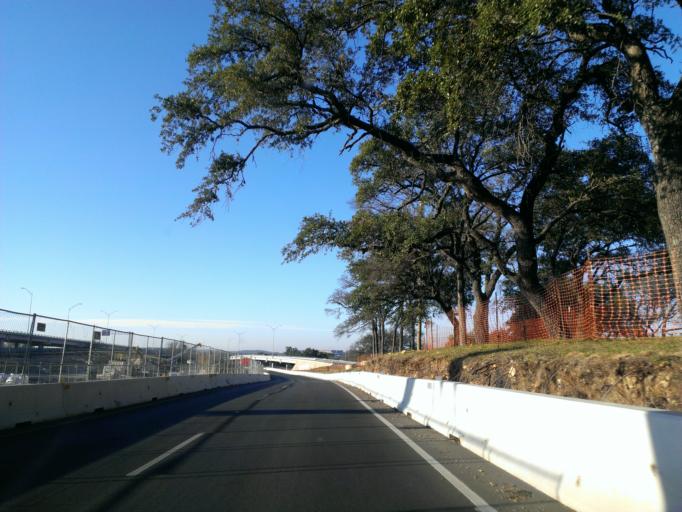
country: US
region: Texas
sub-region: Travis County
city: Rollingwood
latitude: 30.2814
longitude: -97.7672
